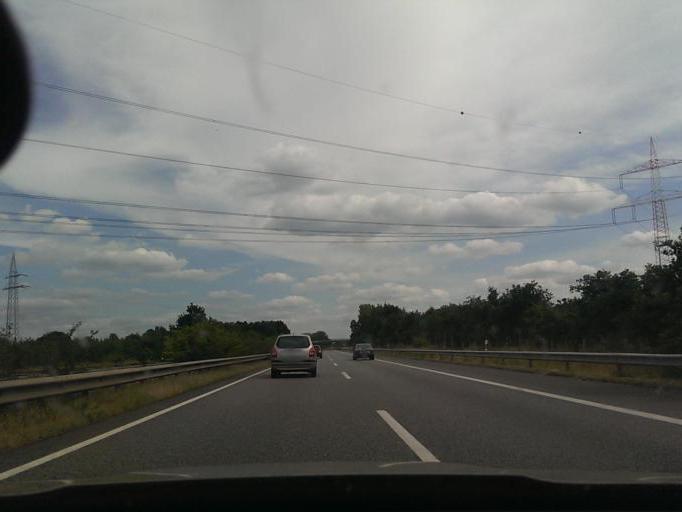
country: DE
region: Lower Saxony
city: Langwedel
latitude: 52.9886
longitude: 9.2036
